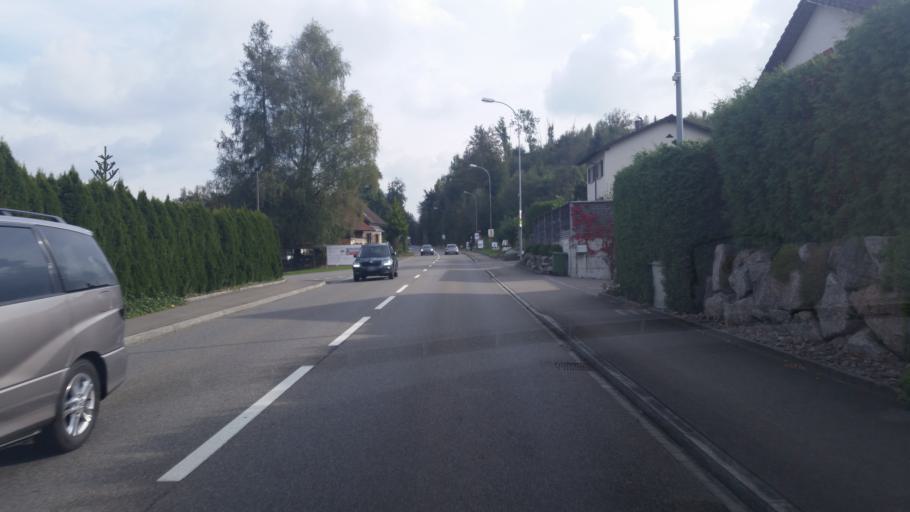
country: CH
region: Aargau
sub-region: Bezirk Baden
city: Kunten
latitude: 47.3661
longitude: 8.3142
